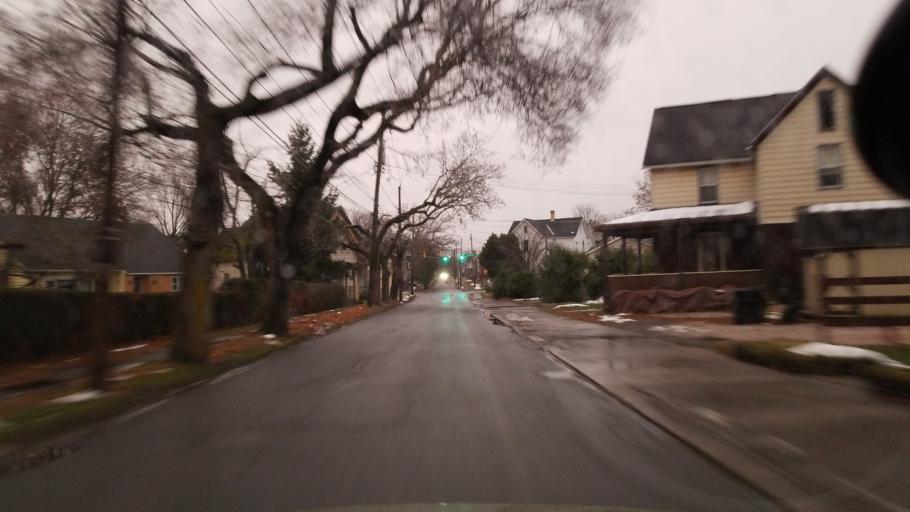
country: US
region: Pennsylvania
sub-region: Clearfield County
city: Clearfield
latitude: 41.0282
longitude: -78.4478
